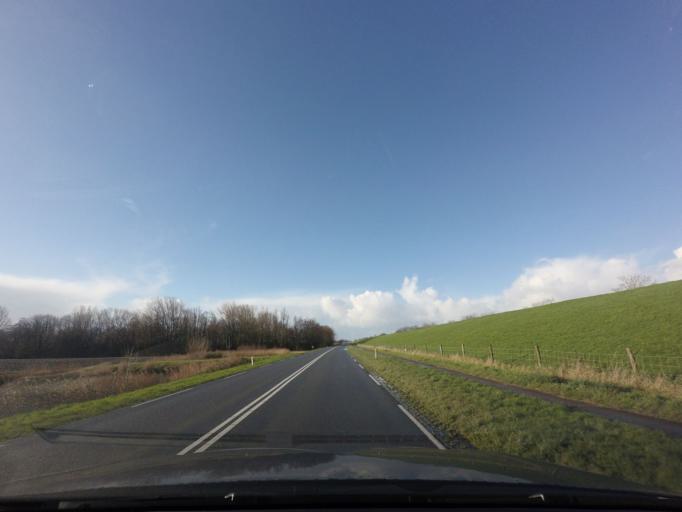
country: NL
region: North Holland
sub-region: Gemeente Opmeer
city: Opmeer
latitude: 52.7521
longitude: 4.9768
